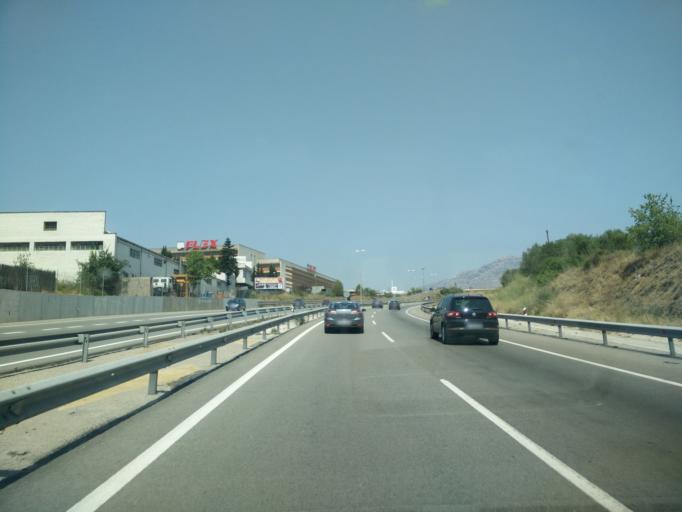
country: ES
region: Catalonia
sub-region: Provincia de Barcelona
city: Esparreguera
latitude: 41.5254
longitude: 1.8820
